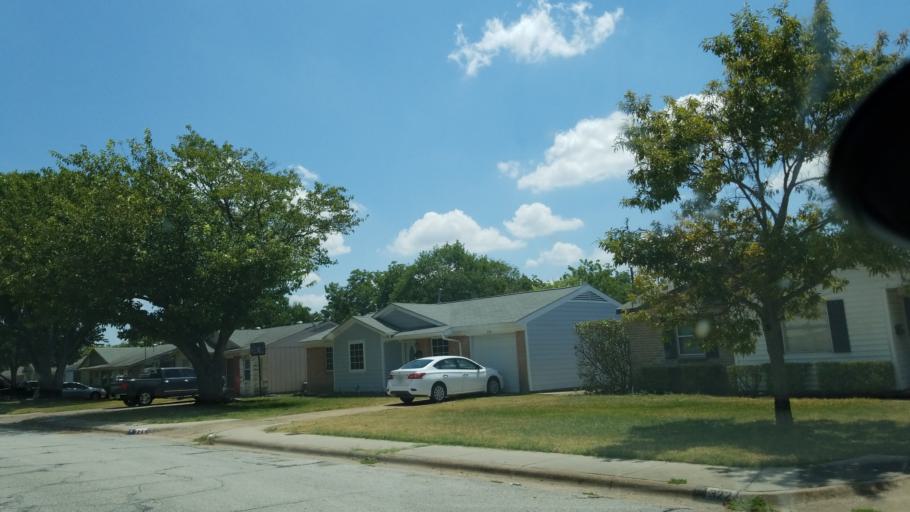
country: US
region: Texas
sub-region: Dallas County
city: Duncanville
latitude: 32.6662
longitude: -96.9027
